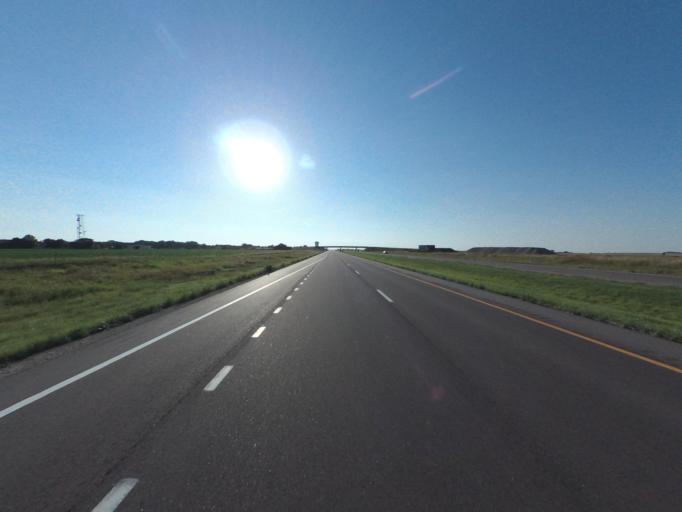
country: US
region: Kansas
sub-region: Ellis County
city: Hays
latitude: 38.8845
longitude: -99.2870
